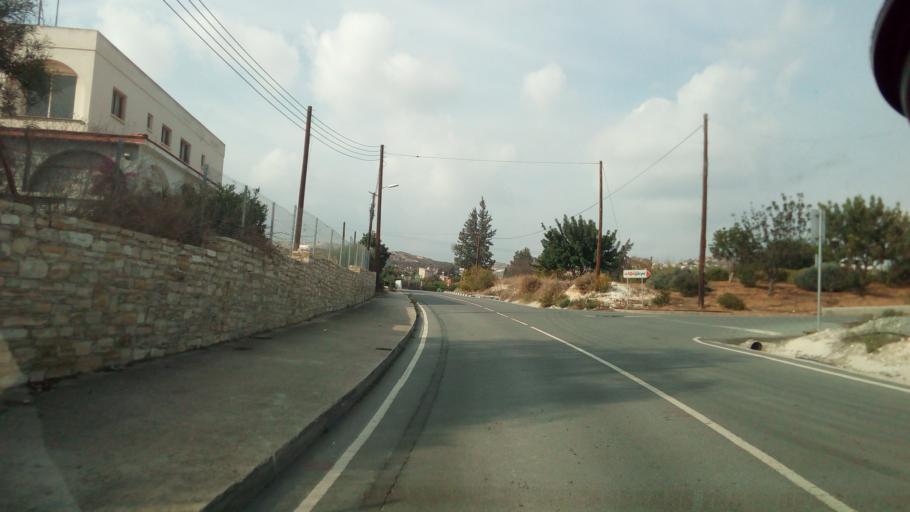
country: CY
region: Larnaka
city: Kofinou
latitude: 34.8168
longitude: 33.3604
